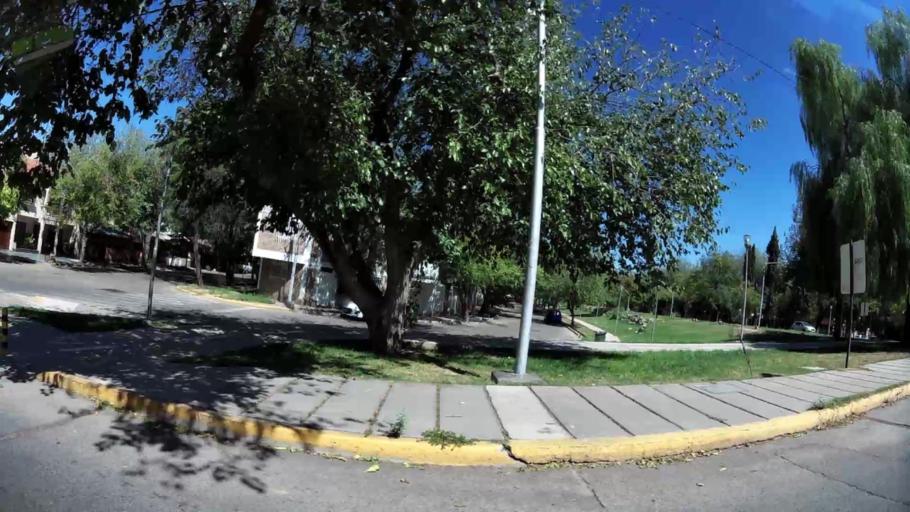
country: AR
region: Mendoza
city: Las Heras
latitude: -32.8625
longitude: -68.8413
